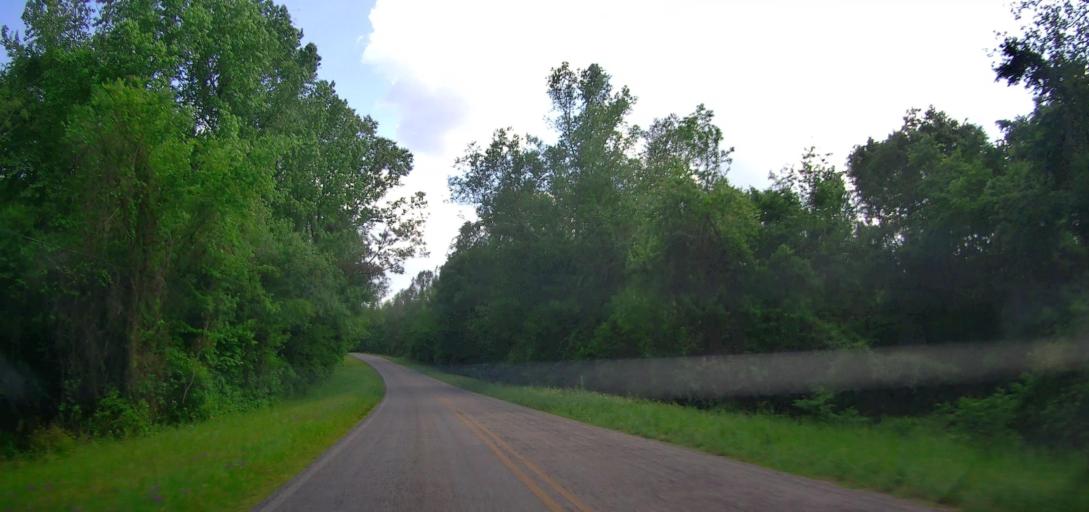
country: US
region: Georgia
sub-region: Laurens County
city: East Dublin
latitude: 32.6715
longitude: -82.8956
